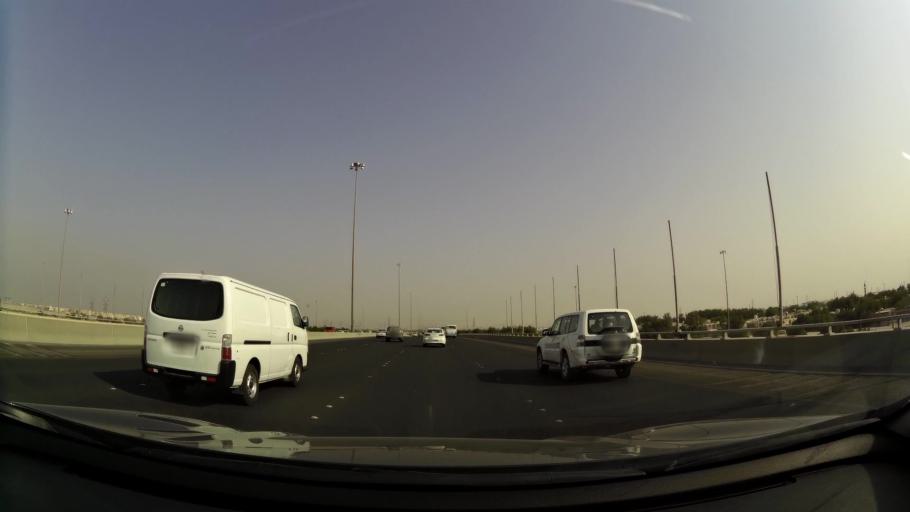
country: KW
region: Muhafazat al Jahra'
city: Al Jahra'
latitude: 29.3235
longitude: 47.7508
